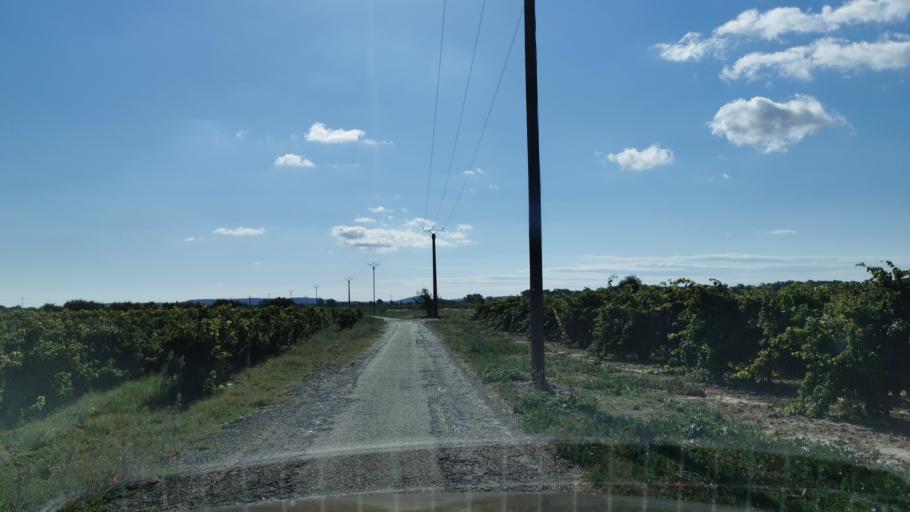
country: FR
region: Languedoc-Roussillon
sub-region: Departement de l'Aude
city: Canet
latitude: 43.2432
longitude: 2.8634
